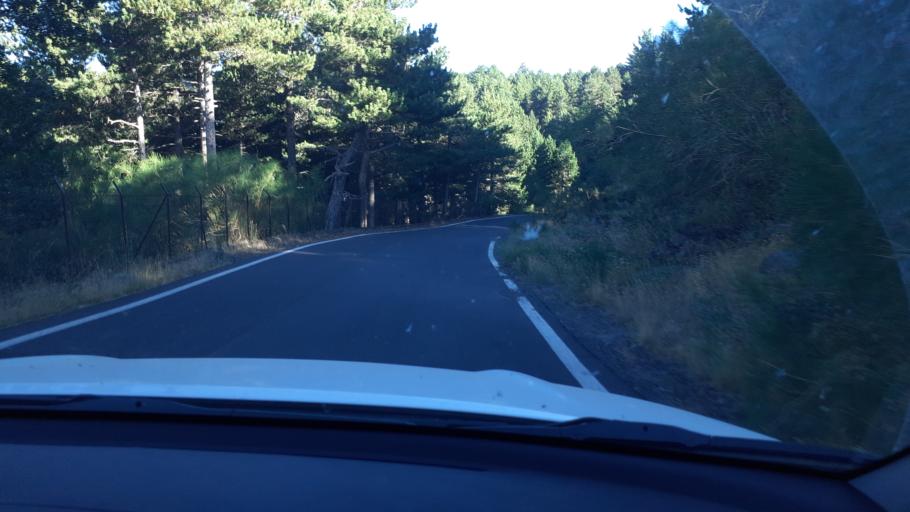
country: IT
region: Sicily
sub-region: Catania
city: Ragalna
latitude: 37.6886
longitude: 14.9766
